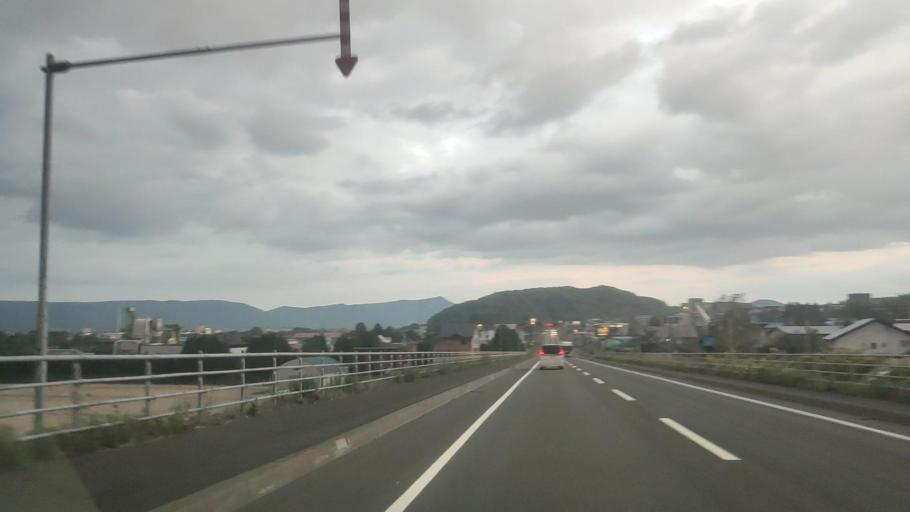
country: JP
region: Hokkaido
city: Shimo-furano
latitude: 43.3529
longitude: 142.3656
